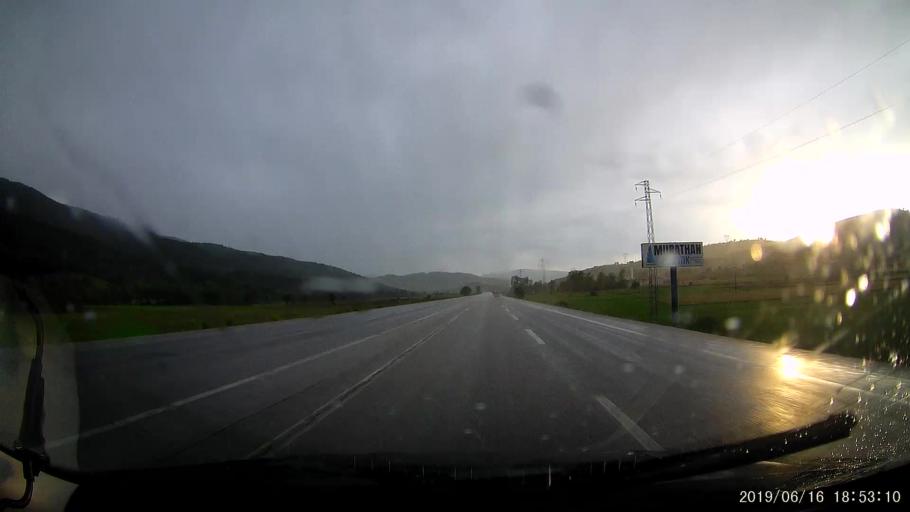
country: TR
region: Erzincan
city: Catalcam
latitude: 39.8995
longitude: 38.8838
